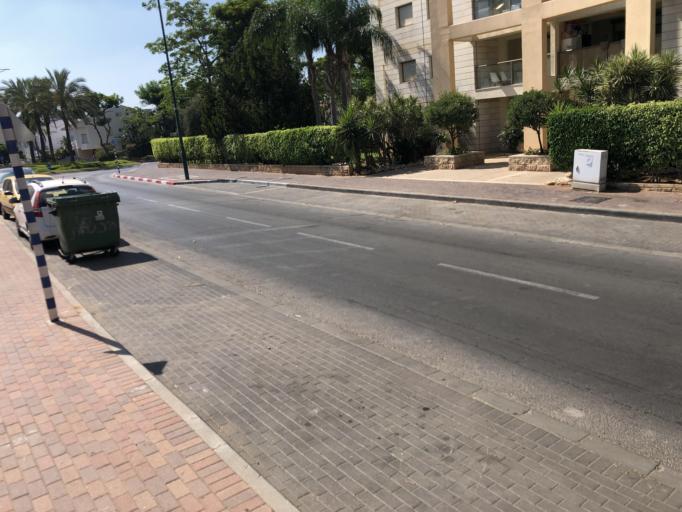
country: IL
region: Central District
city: Yehud
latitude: 32.0354
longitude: 34.8806
